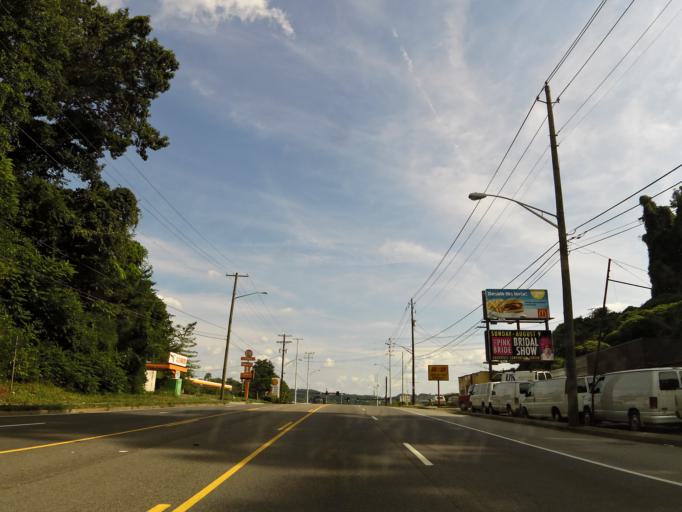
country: US
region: Tennessee
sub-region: Knox County
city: Knoxville
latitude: 35.9463
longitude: -83.9123
